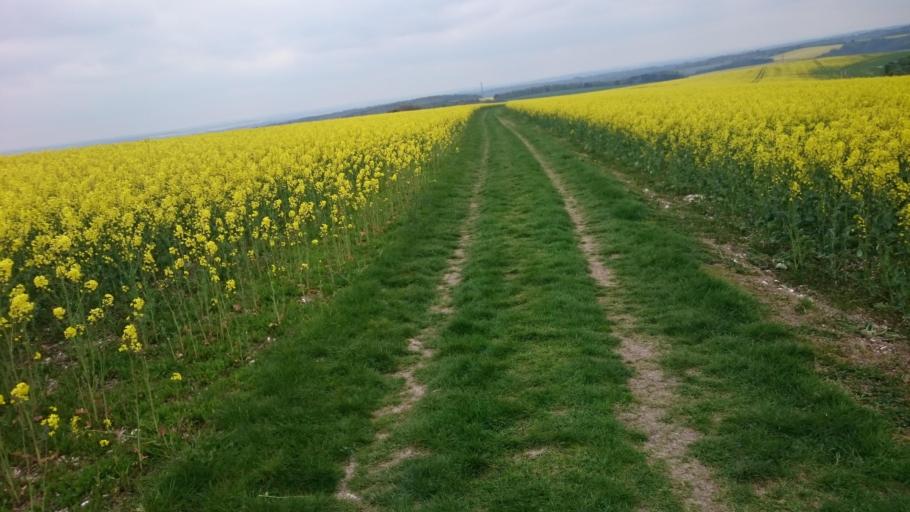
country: GB
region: England
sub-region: Hampshire
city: Highclere
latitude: 51.3074
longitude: -1.3152
